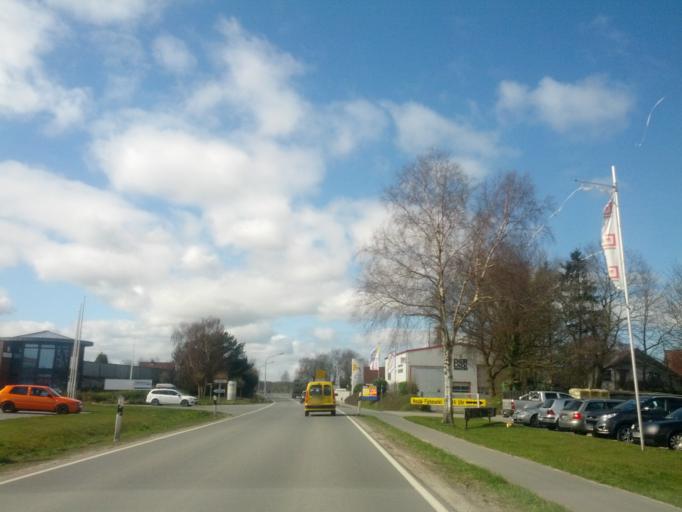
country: DE
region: Lower Saxony
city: Esens
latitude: 53.6330
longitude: 7.6167
